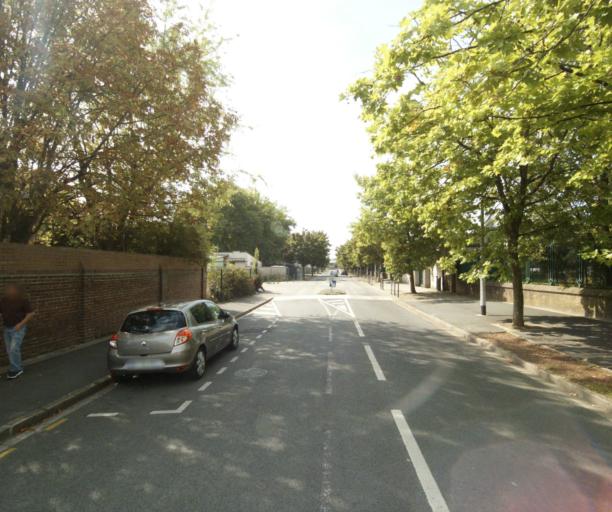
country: FR
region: Nord-Pas-de-Calais
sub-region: Departement du Nord
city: Wattignies
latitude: 50.6078
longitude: 3.0539
